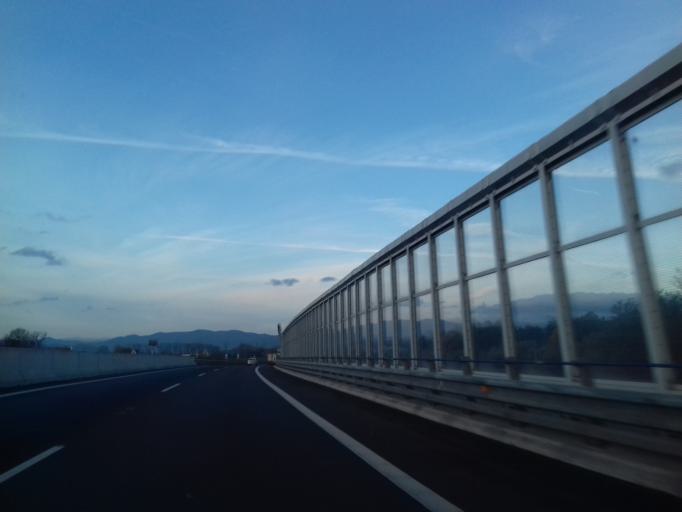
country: SK
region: Banskobystricky
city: Ziar nad Hronom
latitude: 48.5845
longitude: 18.8715
